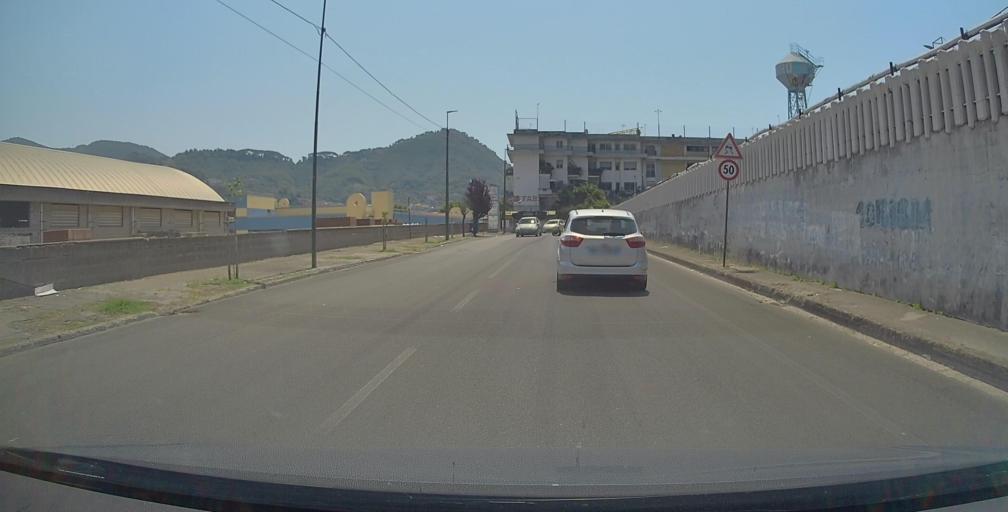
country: IT
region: Campania
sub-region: Provincia di Salerno
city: Cava De Tirreni
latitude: 40.7134
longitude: 14.6993
